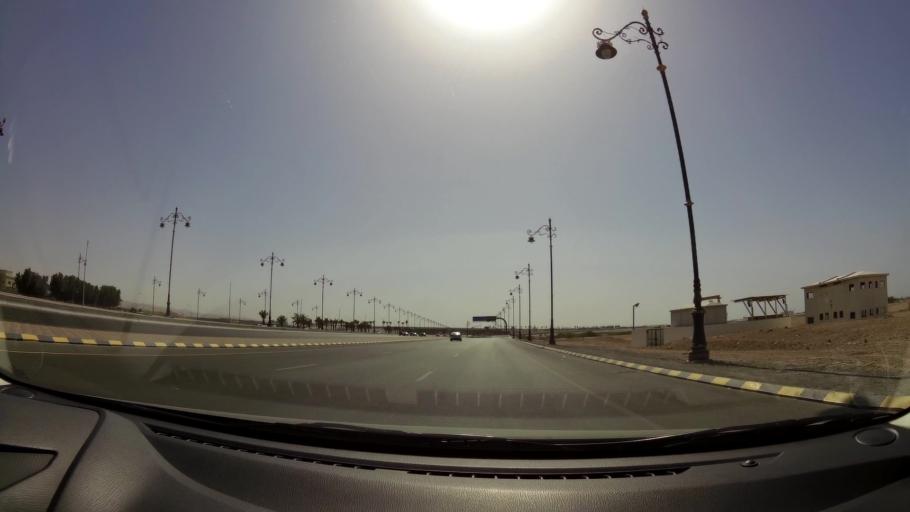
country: OM
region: Muhafazat Masqat
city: Bawshar
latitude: 23.5927
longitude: 58.3436
